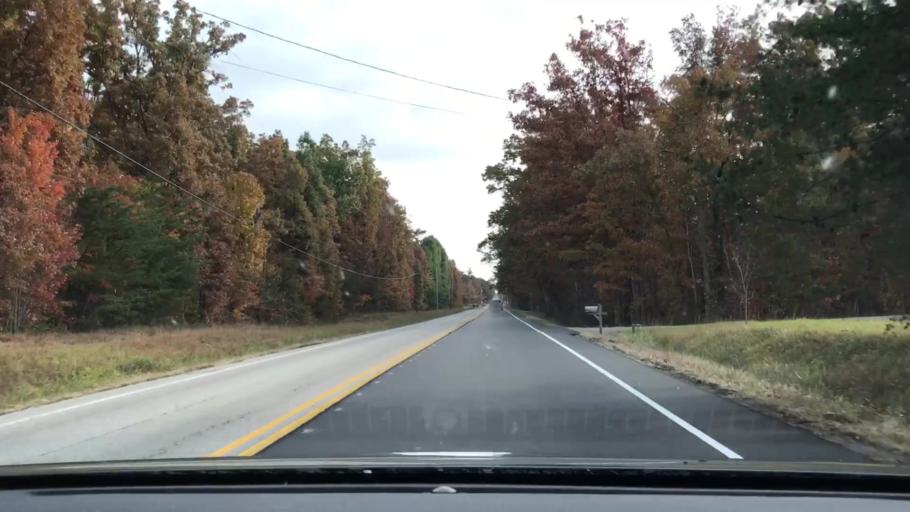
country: US
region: Tennessee
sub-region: Putnam County
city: Monterey
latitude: 36.1229
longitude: -85.1655
